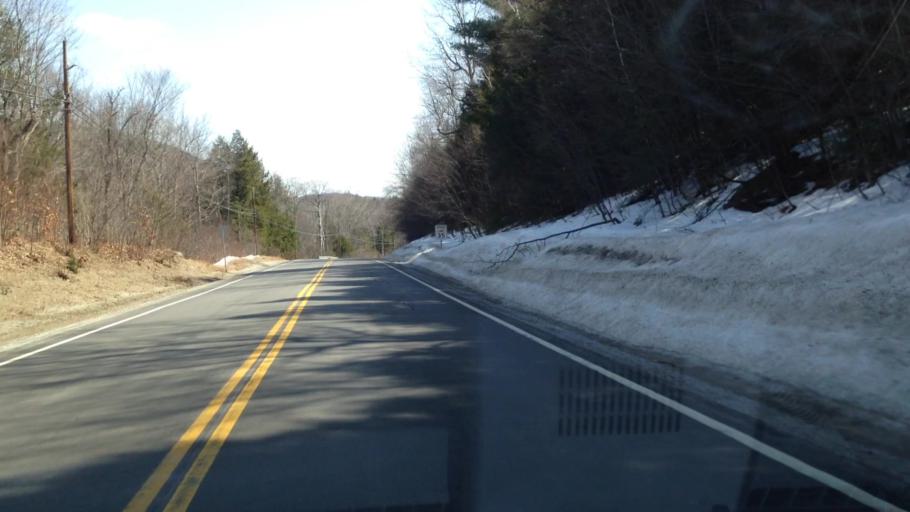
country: US
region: New Hampshire
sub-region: Merrimack County
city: Wilmot
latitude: 43.4630
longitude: -71.9509
